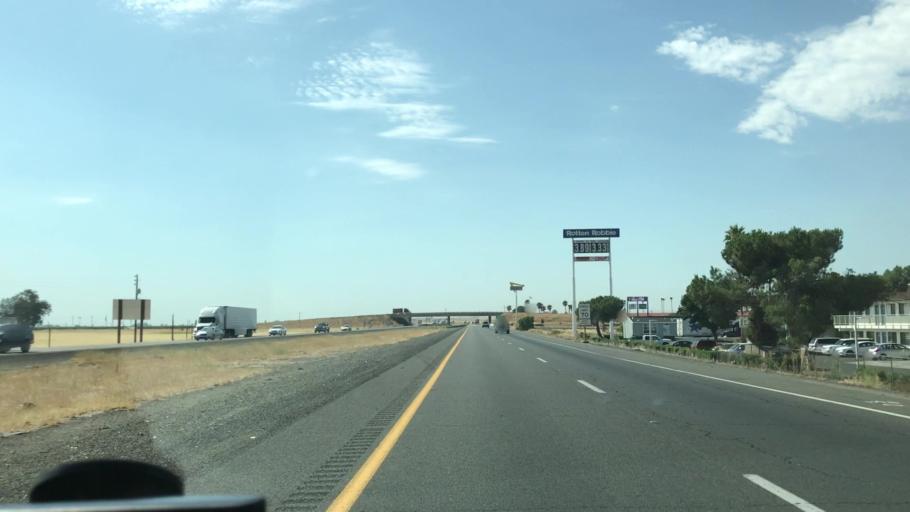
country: US
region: California
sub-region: Merced County
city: Gustine
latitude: 37.1044
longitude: -121.0145
